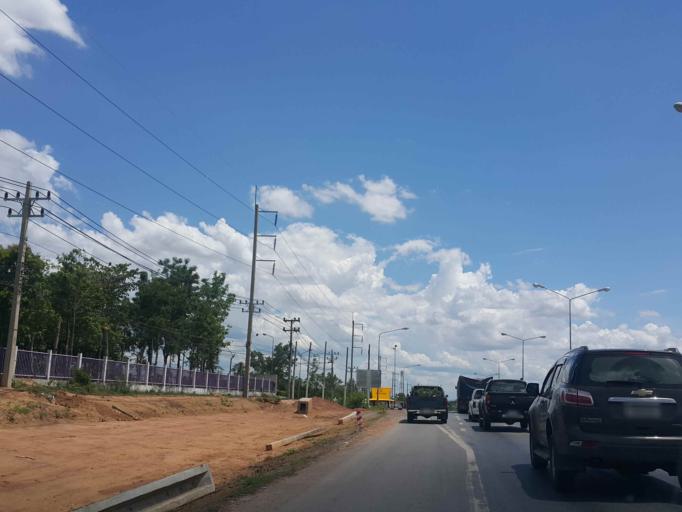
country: TH
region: Phrae
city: Nong Muang Khai
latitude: 18.2048
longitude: 100.1971
